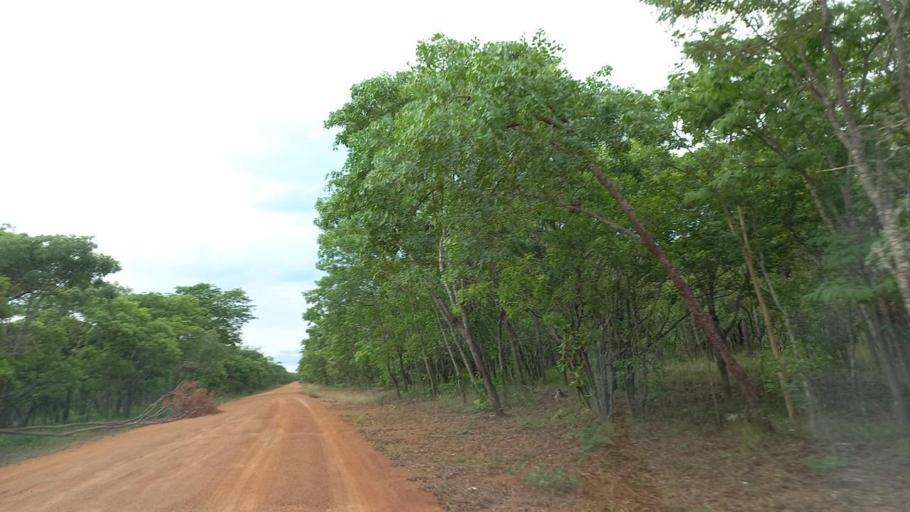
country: ZM
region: North-Western
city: Kalengwa
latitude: -13.3808
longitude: 25.0720
